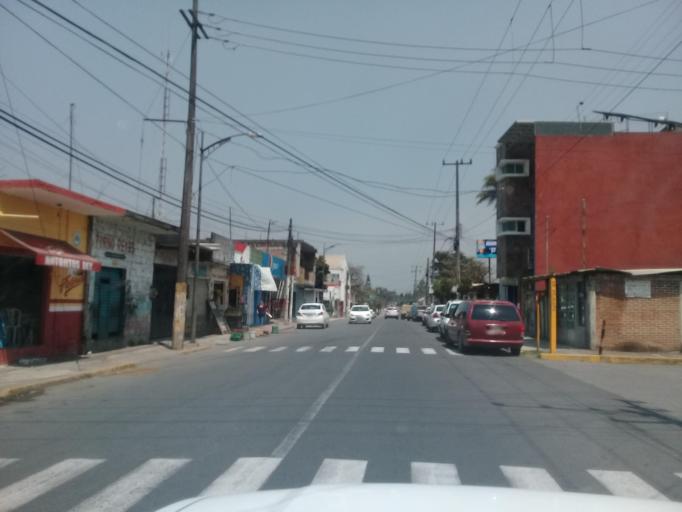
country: MX
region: Veracruz
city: Ixtac Zoquitlan
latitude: 18.8671
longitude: -97.0612
